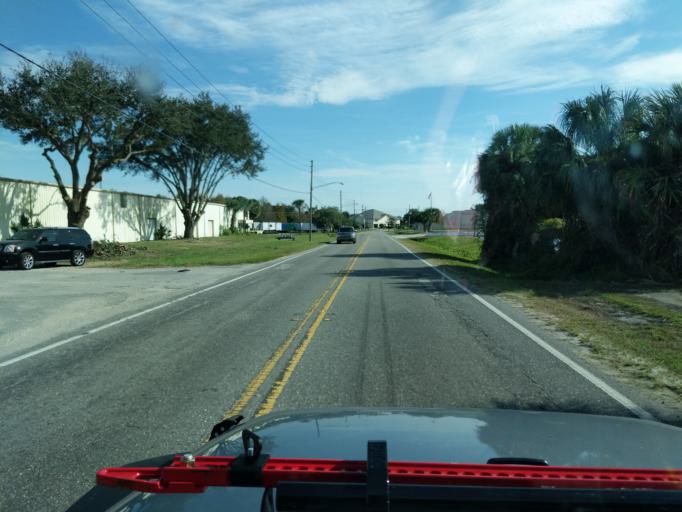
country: US
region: Florida
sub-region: Orange County
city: Ocoee
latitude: 28.5639
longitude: -81.5486
